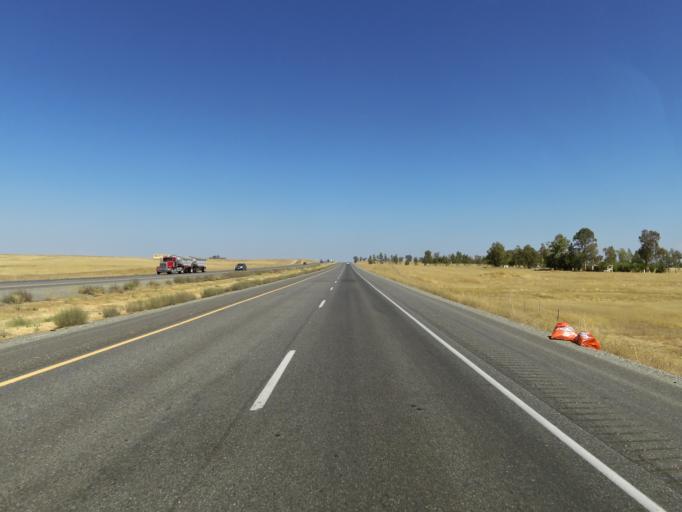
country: US
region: California
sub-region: Tehama County
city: Corning
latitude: 39.8573
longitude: -122.1999
